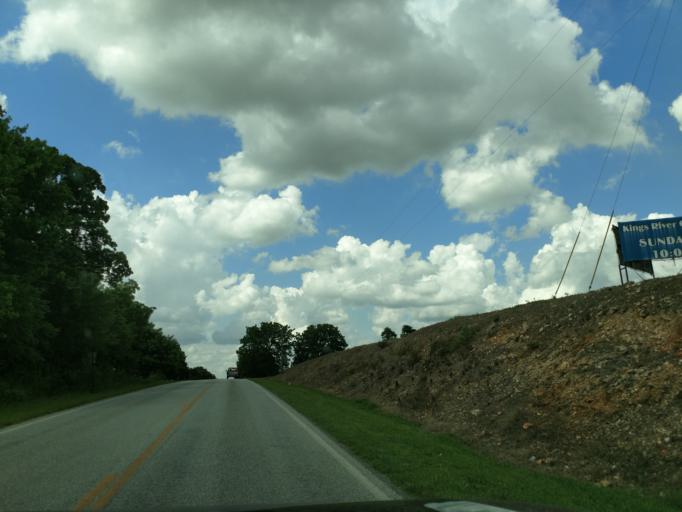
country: US
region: Arkansas
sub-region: Carroll County
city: Berryville
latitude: 36.4019
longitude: -93.5660
